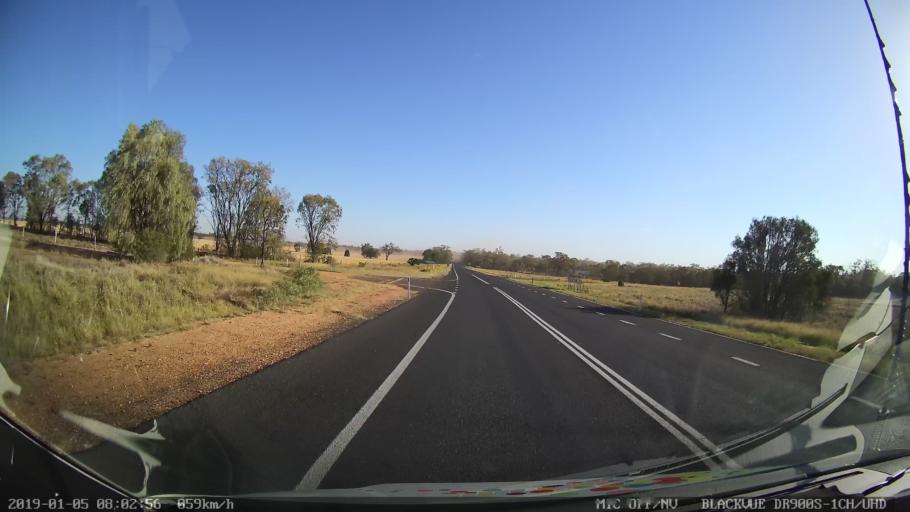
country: AU
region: New South Wales
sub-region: Gilgandra
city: Gilgandra
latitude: -31.6715
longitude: 148.7155
